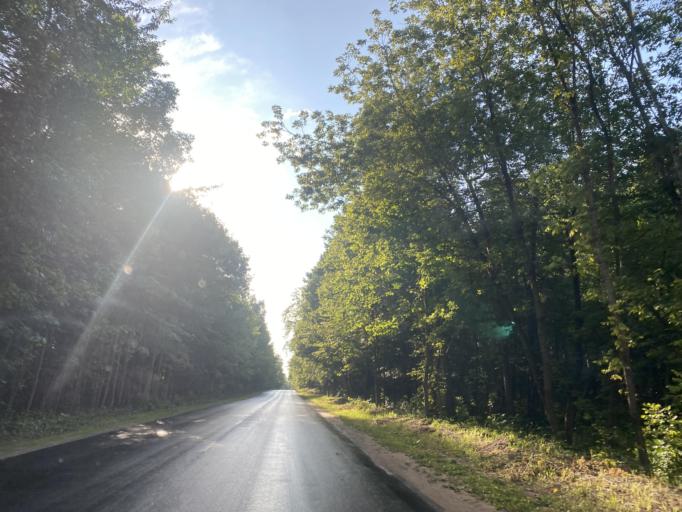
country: BY
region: Minsk
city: Vyaliki Trastsyanets
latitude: 53.9169
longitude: 27.6632
